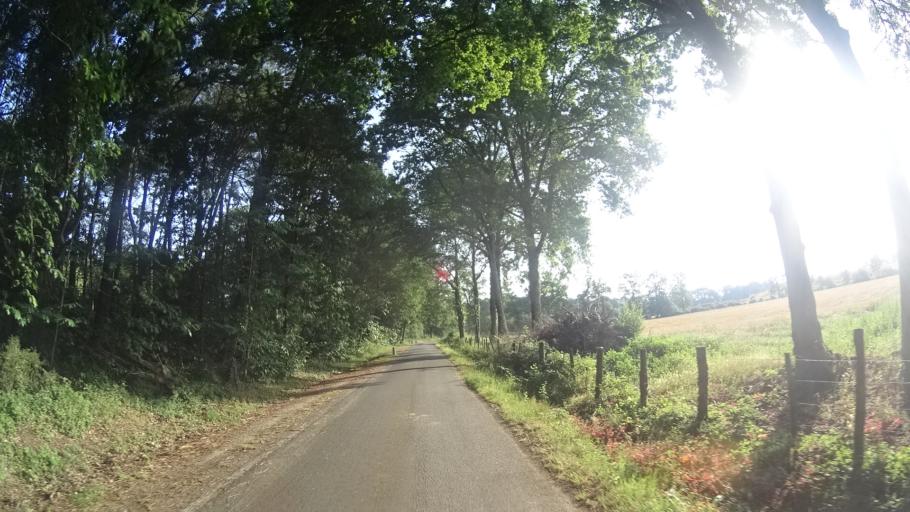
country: FR
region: Brittany
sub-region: Departement d'Ille-et-Vilaine
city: Bains-sur-Oust
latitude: 47.6899
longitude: -2.0608
